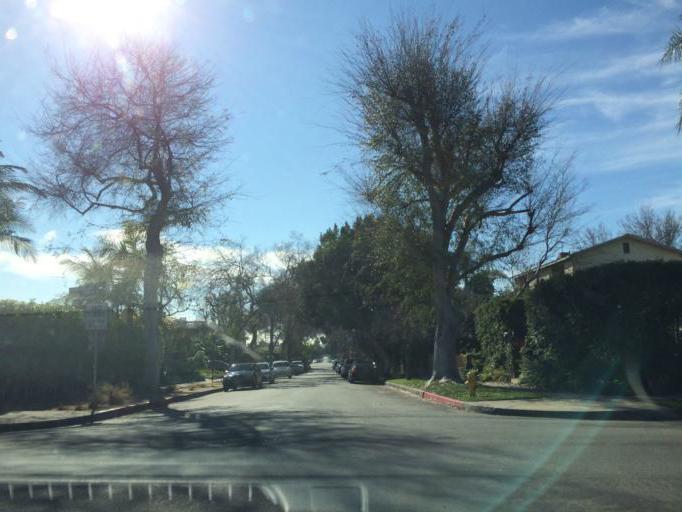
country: US
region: California
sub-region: Los Angeles County
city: West Hollywood
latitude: 34.0855
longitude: -118.3564
